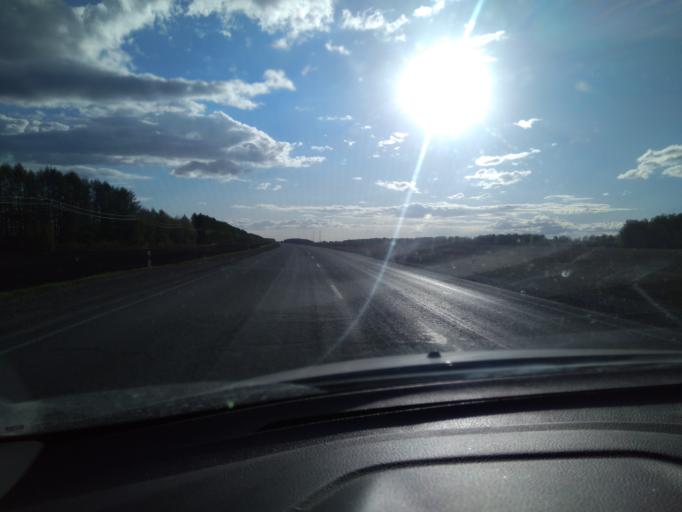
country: RU
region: Sverdlovsk
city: Troitskiy
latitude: 57.0913
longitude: 63.7954
